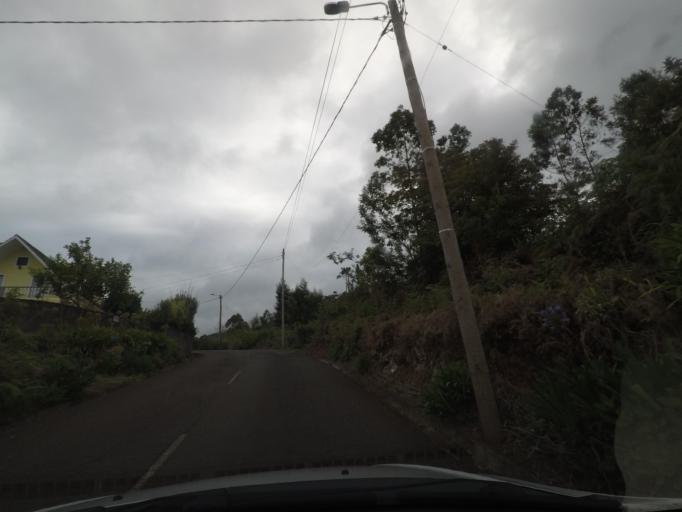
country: PT
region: Madeira
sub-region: Santana
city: Santana
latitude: 32.7870
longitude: -16.8762
